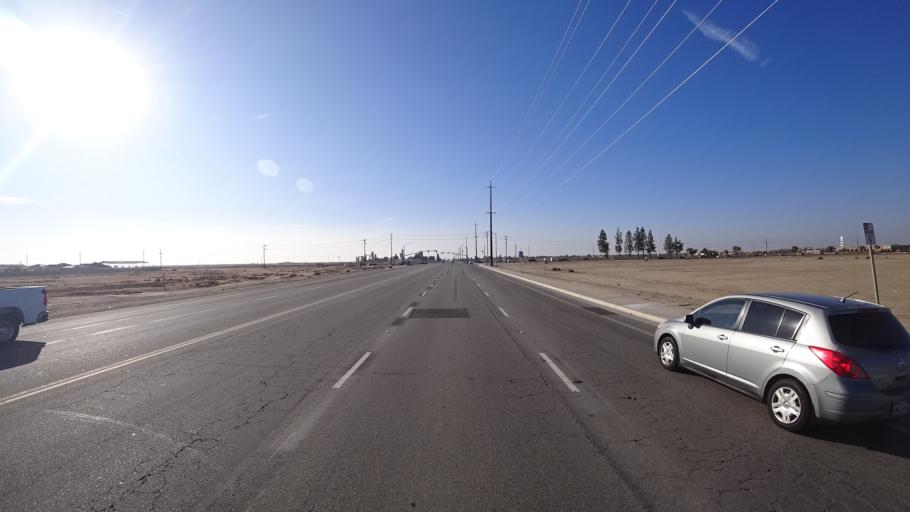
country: US
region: California
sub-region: Kern County
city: Greenacres
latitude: 35.2962
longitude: -119.0896
